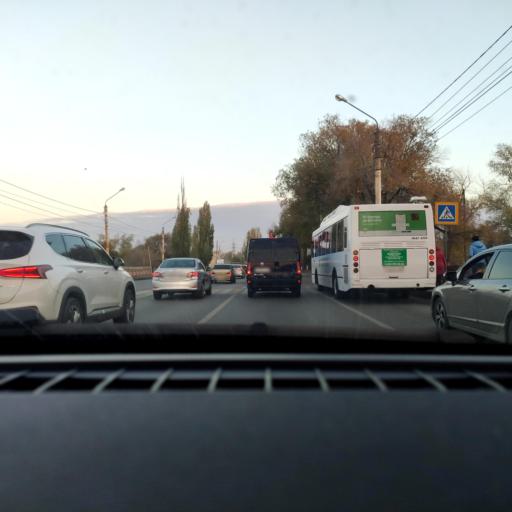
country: RU
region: Voronezj
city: Voronezh
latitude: 51.6268
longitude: 39.2313
